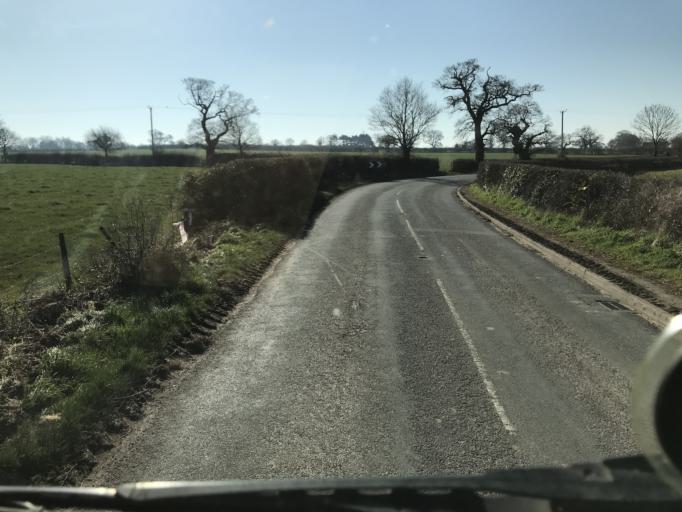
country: GB
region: England
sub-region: Cheshire West and Chester
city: Waverton
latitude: 53.1580
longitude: -2.8294
